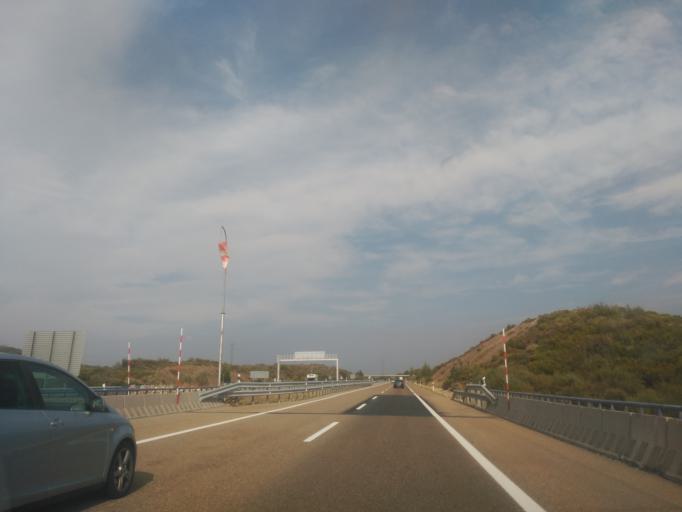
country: ES
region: Castille and Leon
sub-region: Provincia de Zamora
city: Robleda-Cervantes
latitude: 42.0551
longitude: -6.5872
